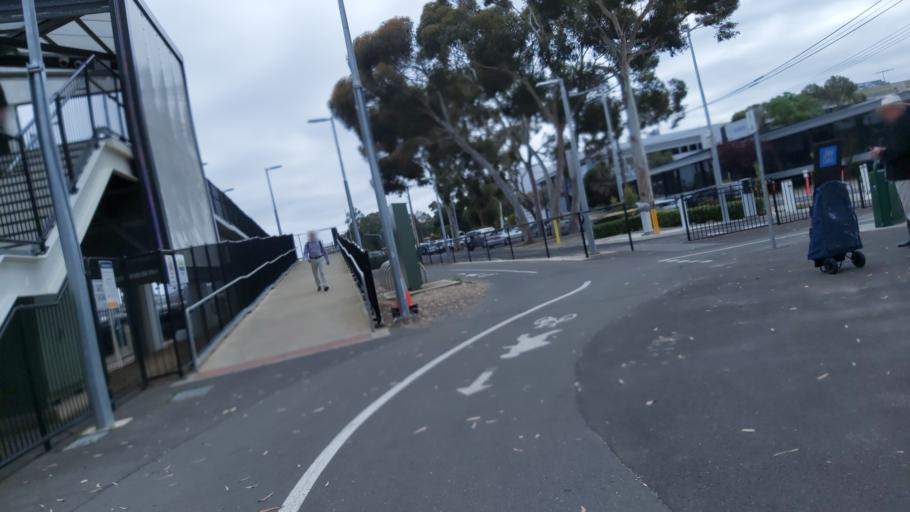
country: AU
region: South Australia
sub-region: Unley
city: Wayville
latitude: -34.9436
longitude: 138.5834
